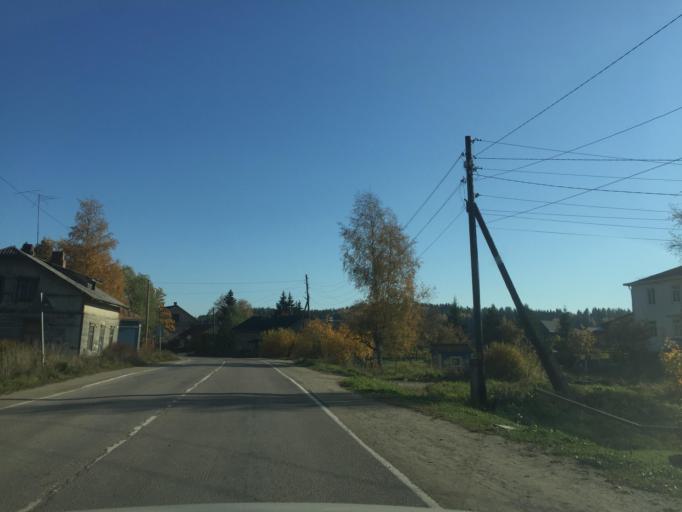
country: RU
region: Leningrad
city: Kuznechnoye
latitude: 61.2986
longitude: 29.8930
